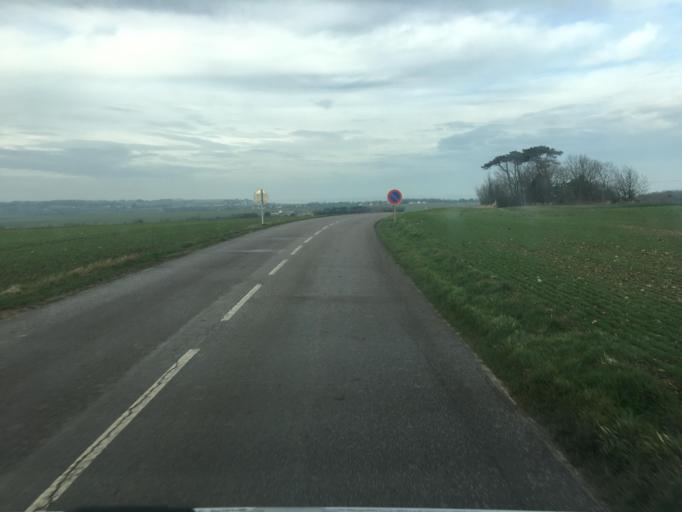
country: FR
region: Lower Normandy
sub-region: Departement du Calvados
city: Ver-sur-Mer
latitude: 49.3219
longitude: -0.5575
